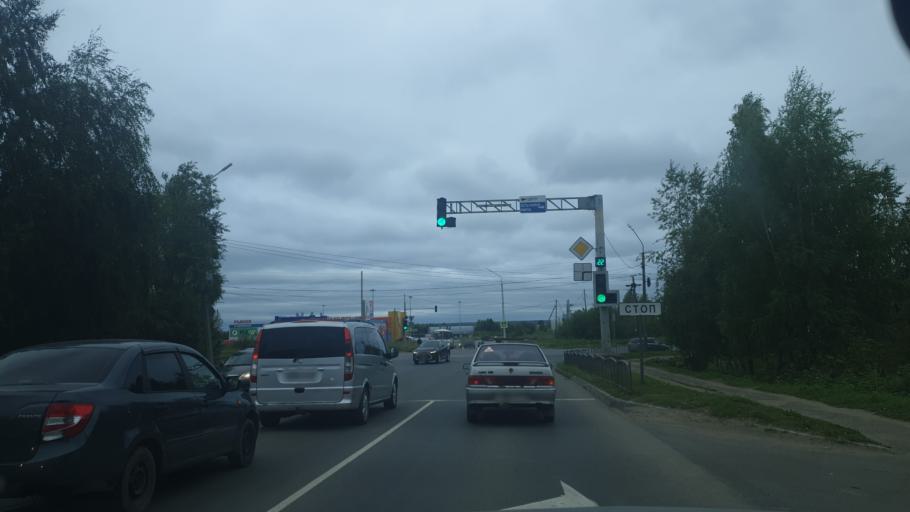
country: RU
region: Komi Republic
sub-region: Syktyvdinskiy Rayon
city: Syktyvkar
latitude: 61.6399
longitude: 50.8141
